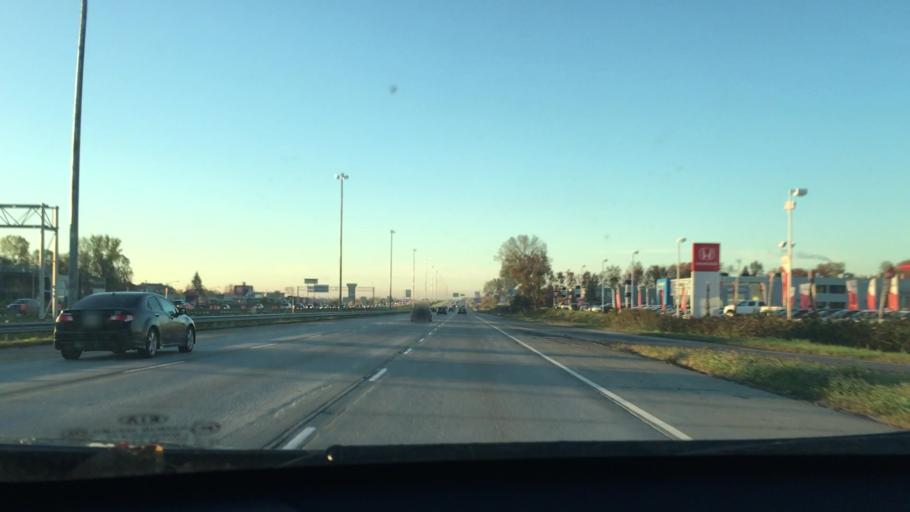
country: CA
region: Quebec
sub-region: Laurentides
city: Saint-Jerome
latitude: 45.7750
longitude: -74.0209
